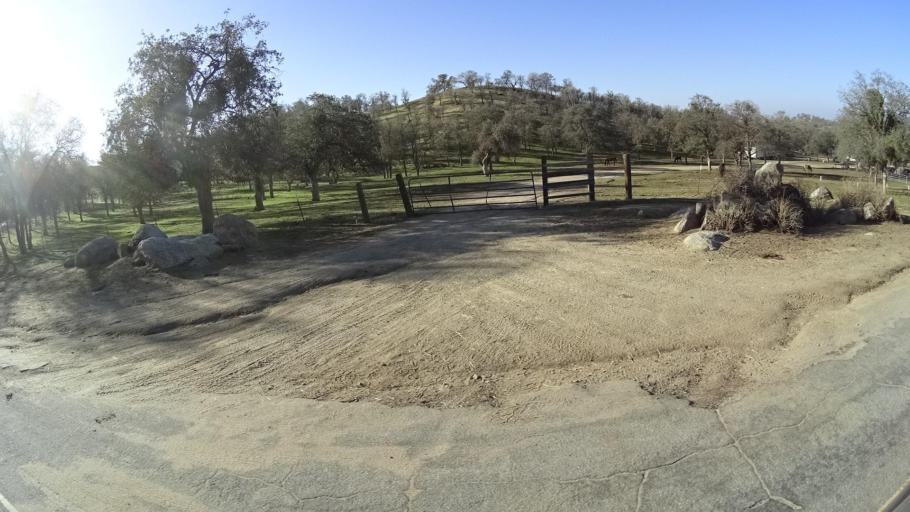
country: US
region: California
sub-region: Kern County
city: Alta Sierra
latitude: 35.7487
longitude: -118.8181
